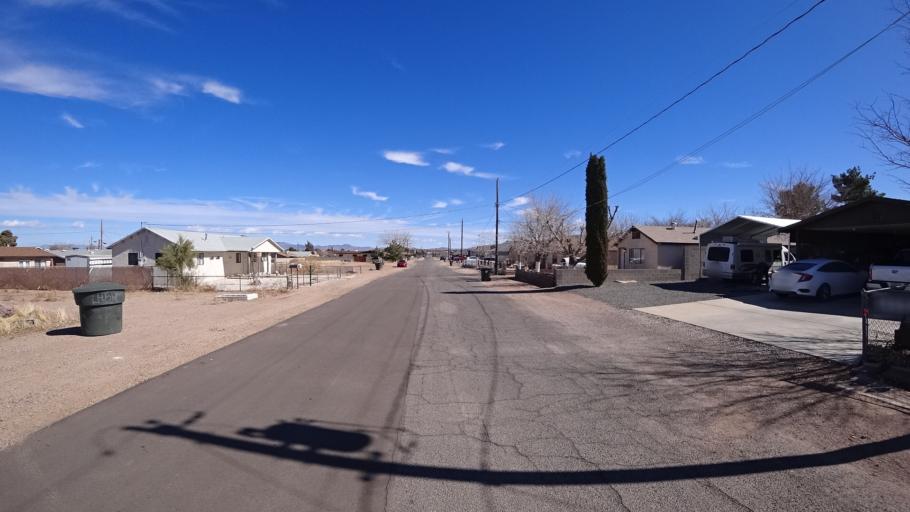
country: US
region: Arizona
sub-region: Mohave County
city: Kingman
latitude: 35.2052
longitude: -114.0399
